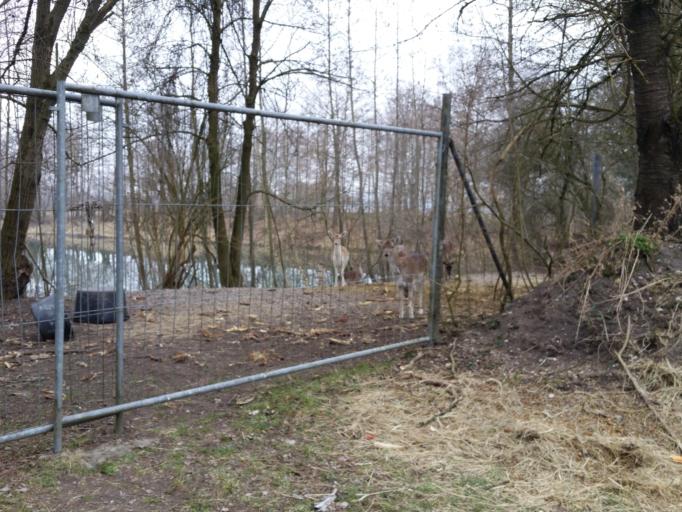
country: DE
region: Bavaria
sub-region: Upper Bavaria
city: Langenpreising
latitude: 48.4215
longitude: 11.9513
